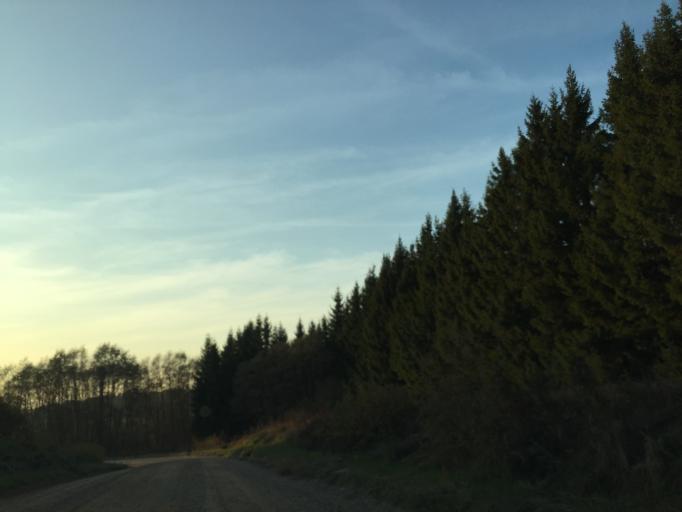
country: LV
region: Vainode
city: Vainode
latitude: 56.4896
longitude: 21.7796
